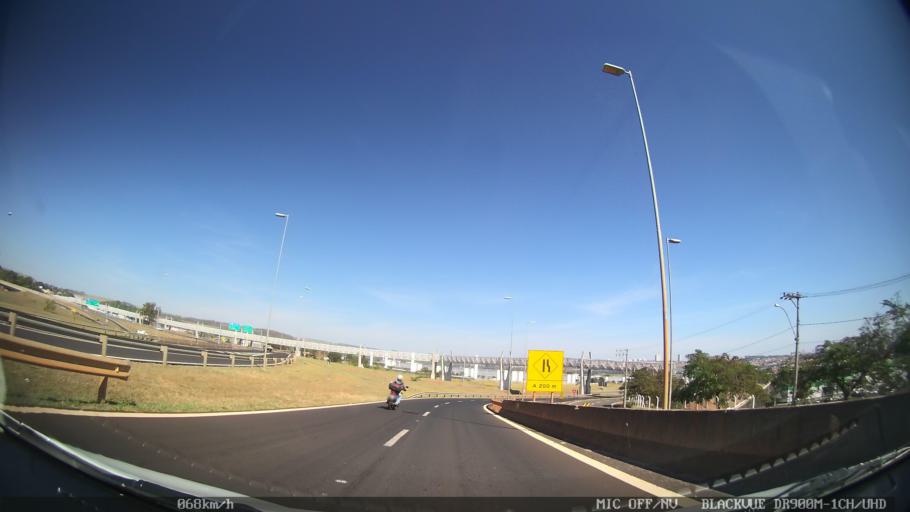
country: BR
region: Sao Paulo
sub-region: Ribeirao Preto
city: Ribeirao Preto
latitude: -21.2058
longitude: -47.7604
